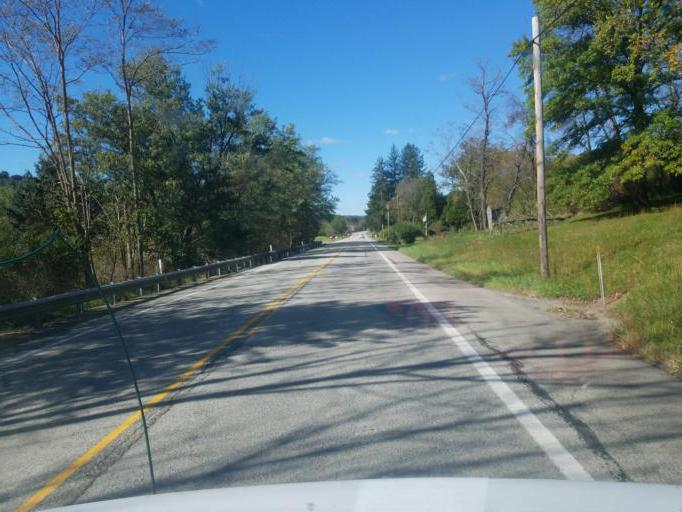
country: US
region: Pennsylvania
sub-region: Westmoreland County
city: Ligonier
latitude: 40.2147
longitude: -79.2037
